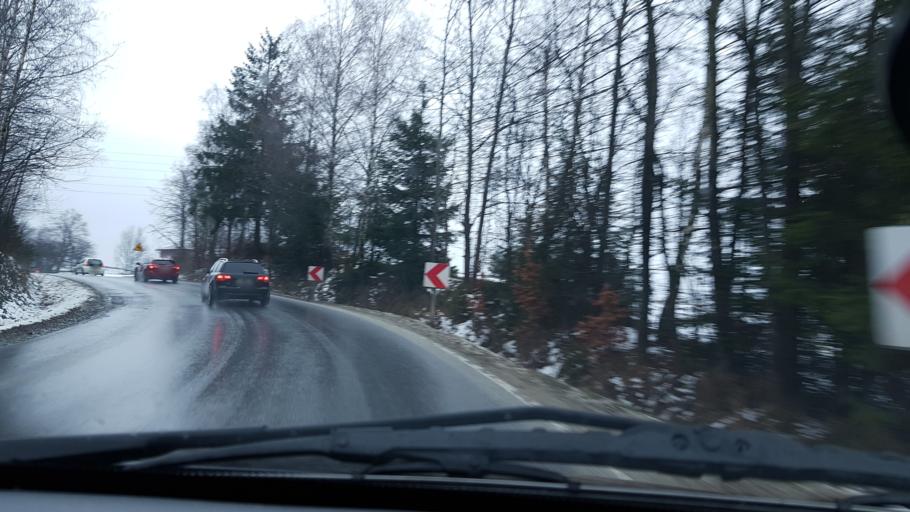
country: PL
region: Lesser Poland Voivodeship
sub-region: Powiat nowotarski
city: Sieniawa
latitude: 49.5134
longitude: 19.8915
